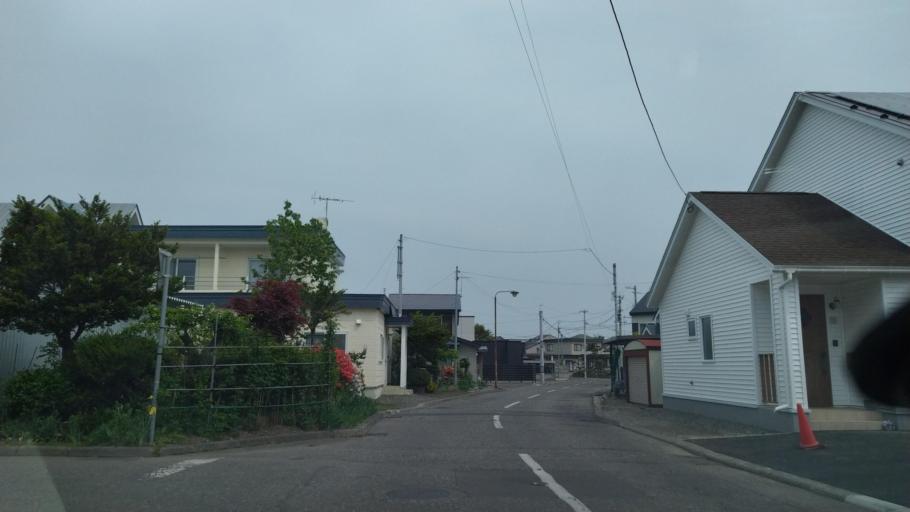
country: JP
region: Hokkaido
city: Obihiro
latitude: 42.9138
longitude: 143.0607
